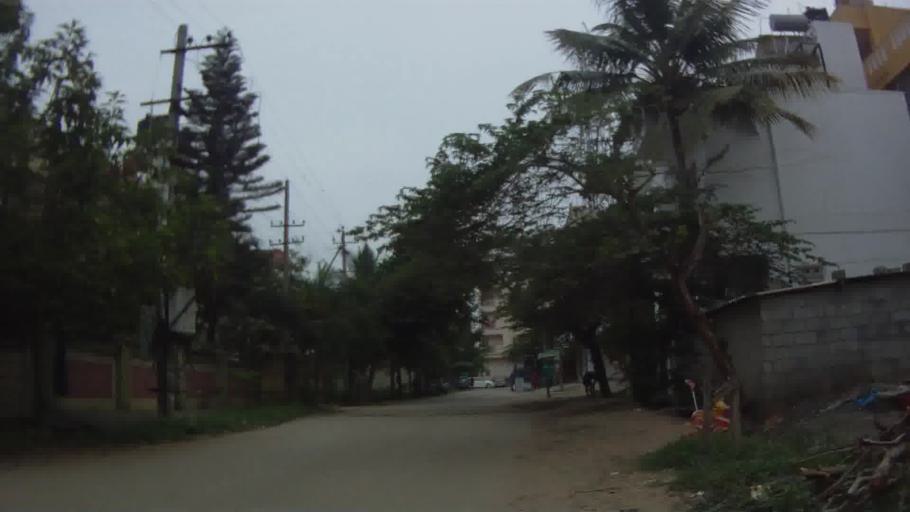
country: IN
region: Karnataka
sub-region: Bangalore Urban
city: Bangalore
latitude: 12.9598
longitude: 77.7185
